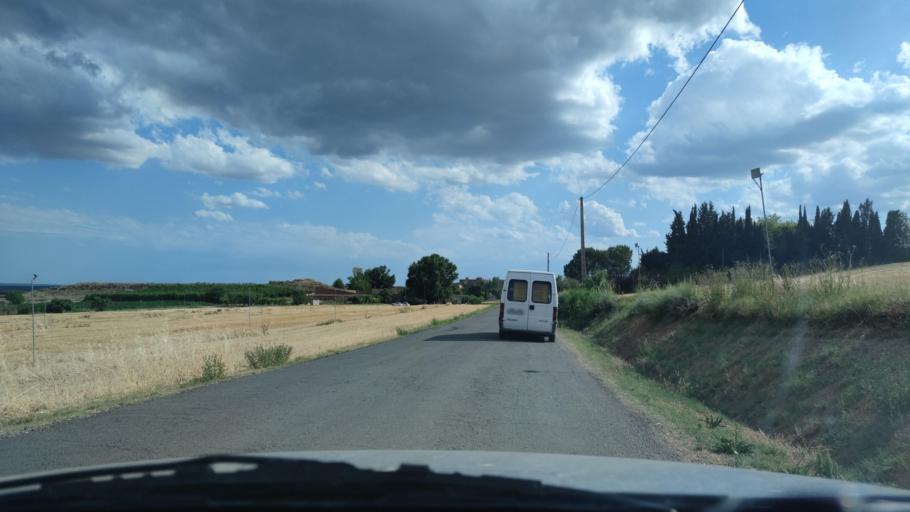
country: ES
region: Catalonia
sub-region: Provincia de Lleida
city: Alcarras
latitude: 41.5745
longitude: 0.5319
